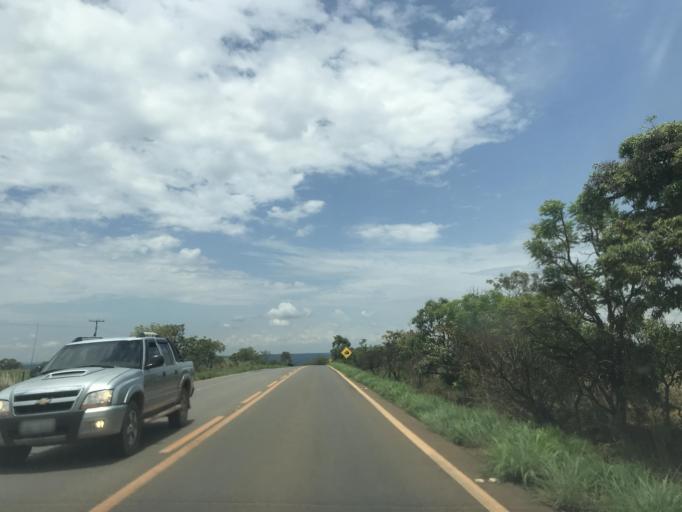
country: BR
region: Goias
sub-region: Luziania
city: Luziania
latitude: -16.3489
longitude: -48.0360
